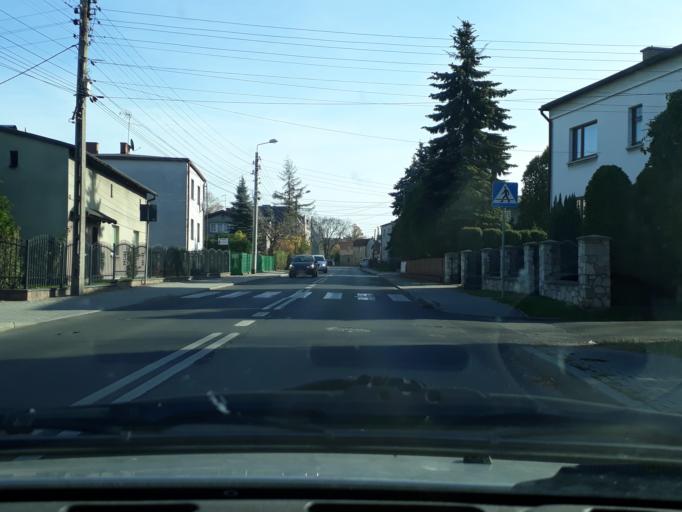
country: PL
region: Silesian Voivodeship
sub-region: Powiat tarnogorski
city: Tarnowskie Gory
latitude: 50.4235
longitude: 18.8702
